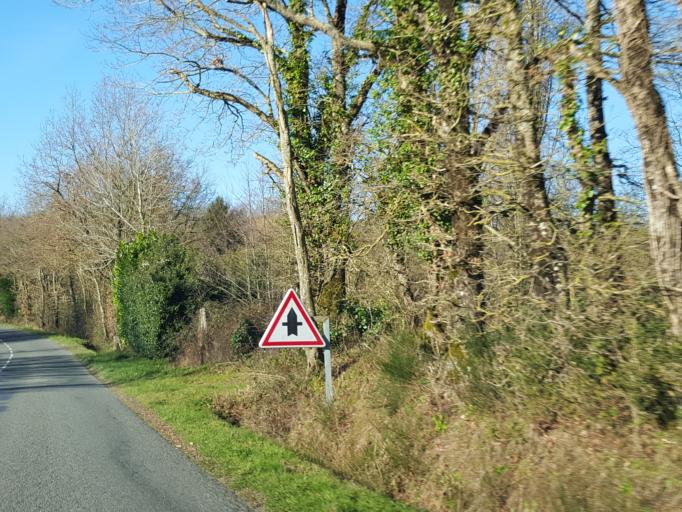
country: FR
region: Pays de la Loire
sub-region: Departement de la Vendee
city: Venansault
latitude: 46.6724
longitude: -1.4788
